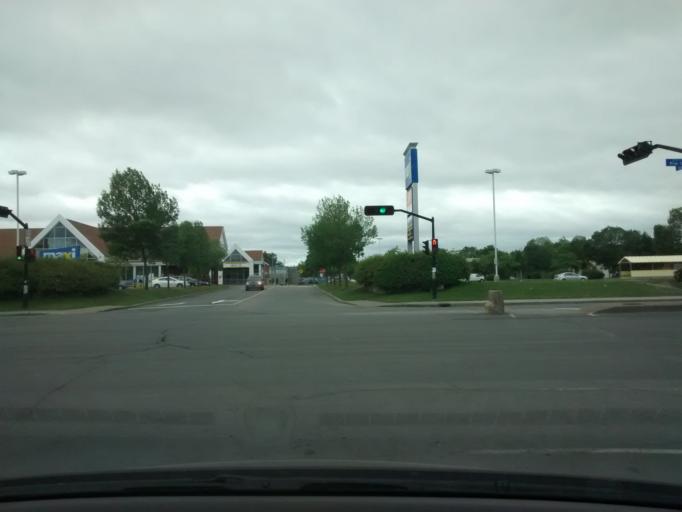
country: CA
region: Quebec
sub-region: Montreal
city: Saint-Leonard
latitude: 45.5853
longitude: -73.6310
